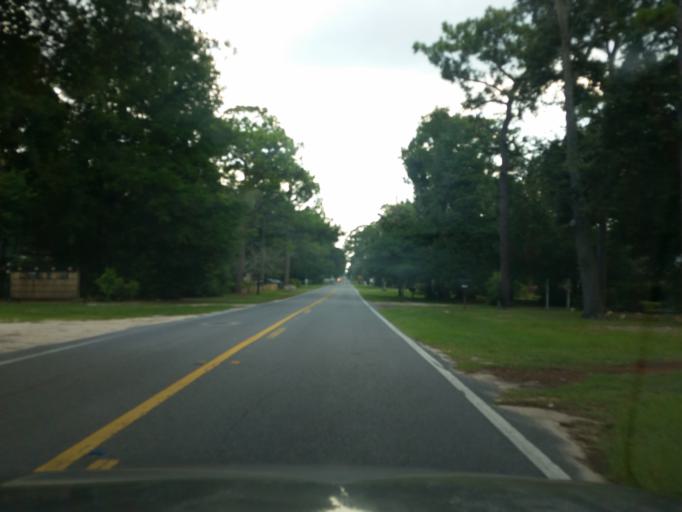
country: US
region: Florida
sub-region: Escambia County
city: Ferry Pass
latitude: 30.4937
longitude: -87.2060
